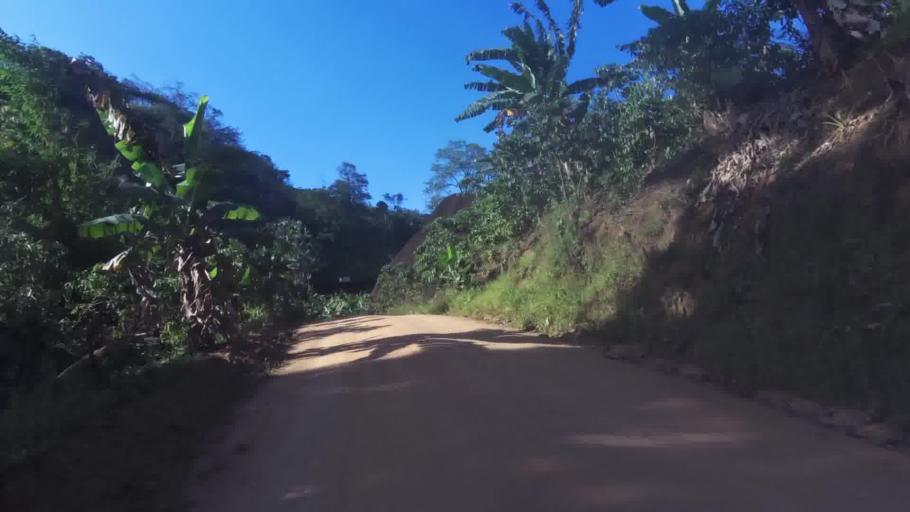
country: BR
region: Espirito Santo
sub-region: Iconha
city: Iconha
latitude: -20.7586
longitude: -40.8186
